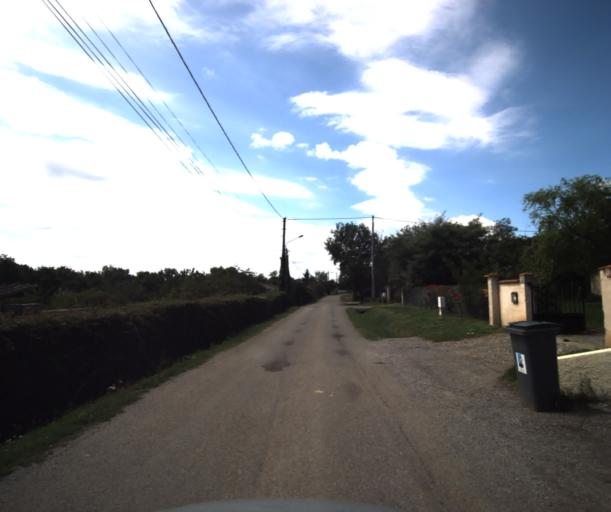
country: FR
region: Midi-Pyrenees
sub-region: Departement de la Haute-Garonne
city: Lacasse
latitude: 43.3901
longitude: 1.2627
